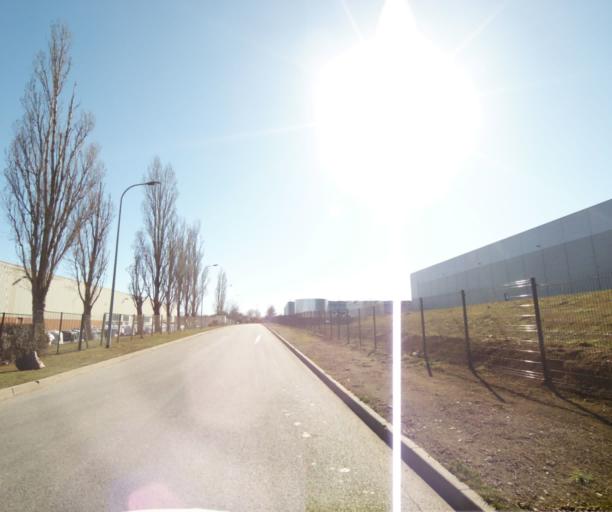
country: FR
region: Lorraine
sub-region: Departement de Meurthe-et-Moselle
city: Fleville-devant-Nancy
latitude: 48.6119
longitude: 6.1974
